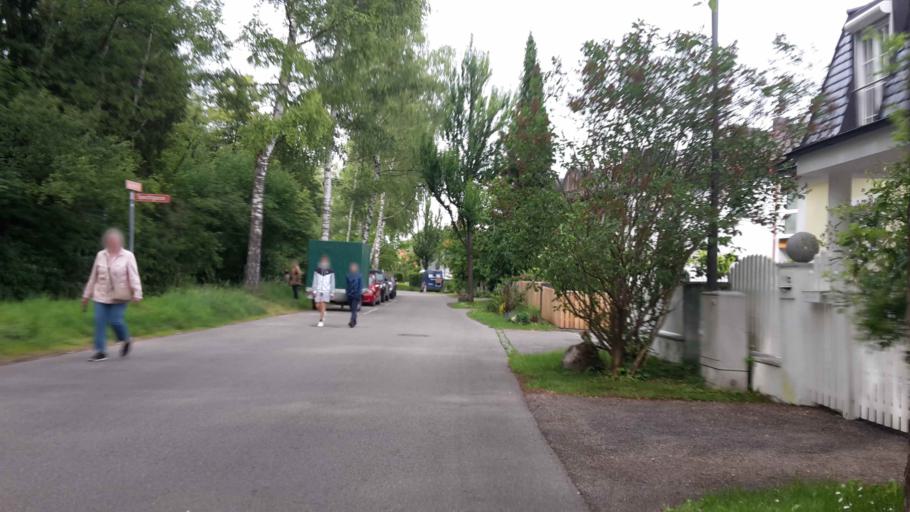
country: DE
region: Bavaria
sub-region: Upper Bavaria
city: Dachau
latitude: 48.2415
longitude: 11.4384
